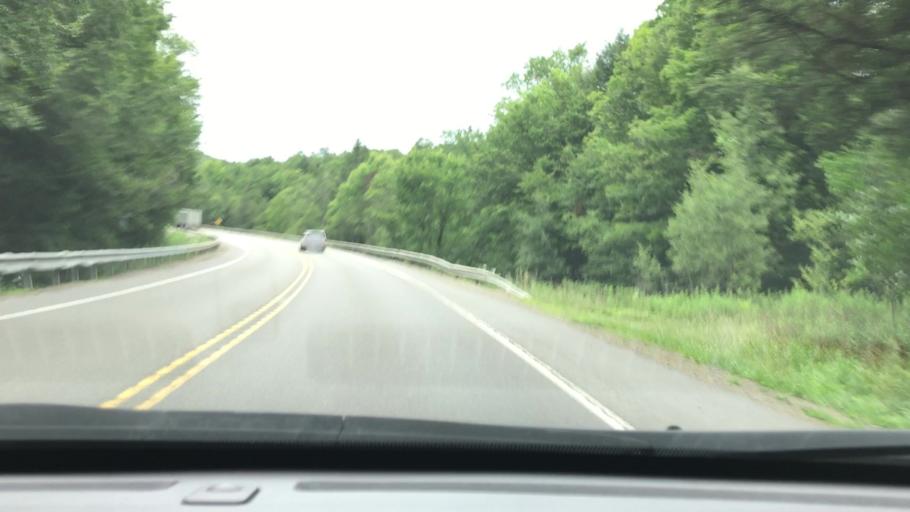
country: US
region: Pennsylvania
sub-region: McKean County
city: Kane
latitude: 41.6691
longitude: -78.6803
